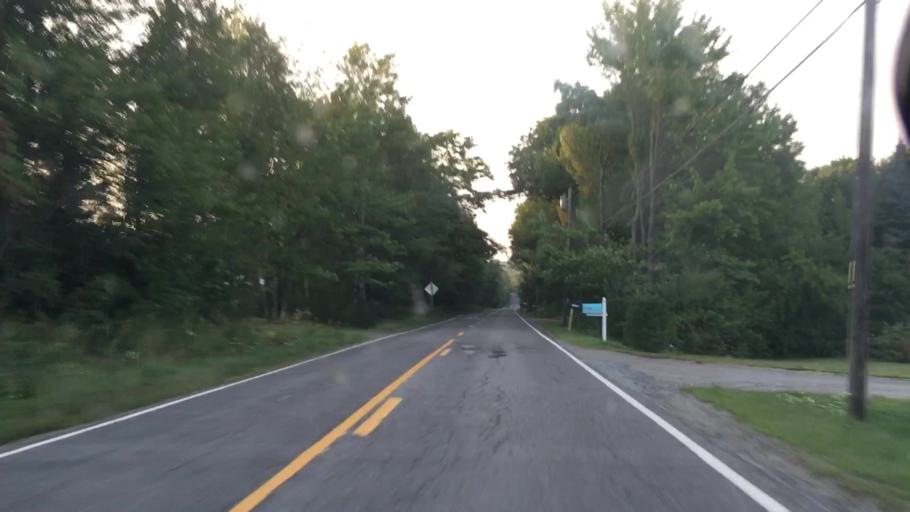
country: US
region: Maine
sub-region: Waldo County
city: Frankfort
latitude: 44.6996
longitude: -68.9451
